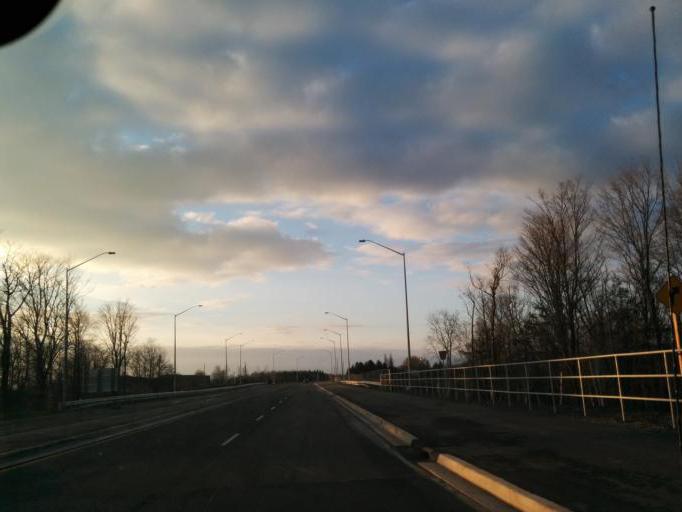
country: CA
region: Ontario
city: Brampton
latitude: 43.8767
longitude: -79.7630
